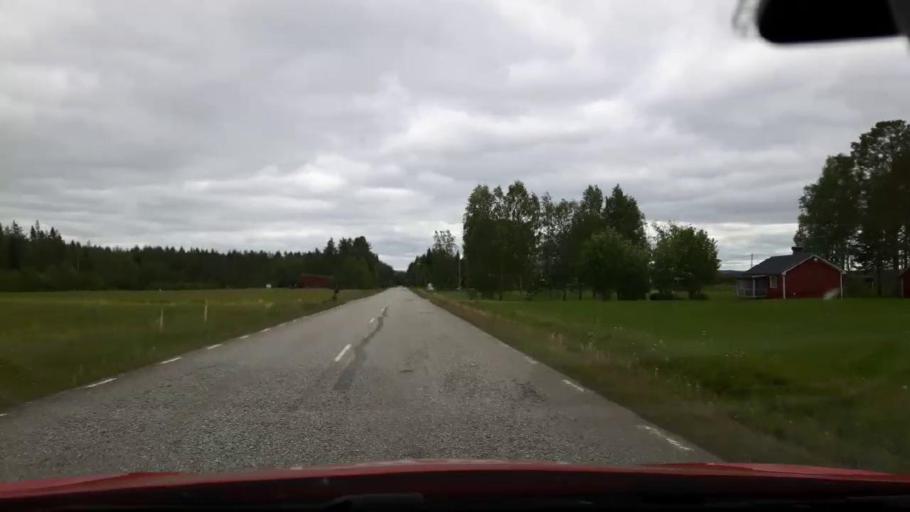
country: SE
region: Jaemtland
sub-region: Ragunda Kommun
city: Hammarstrand
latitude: 63.2276
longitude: 15.9283
